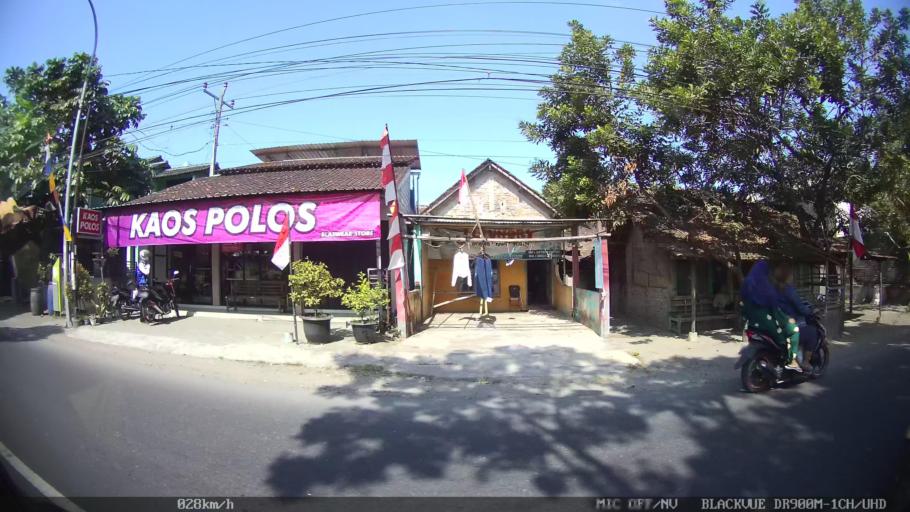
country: ID
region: Daerah Istimewa Yogyakarta
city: Sewon
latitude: -7.8809
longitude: 110.3898
